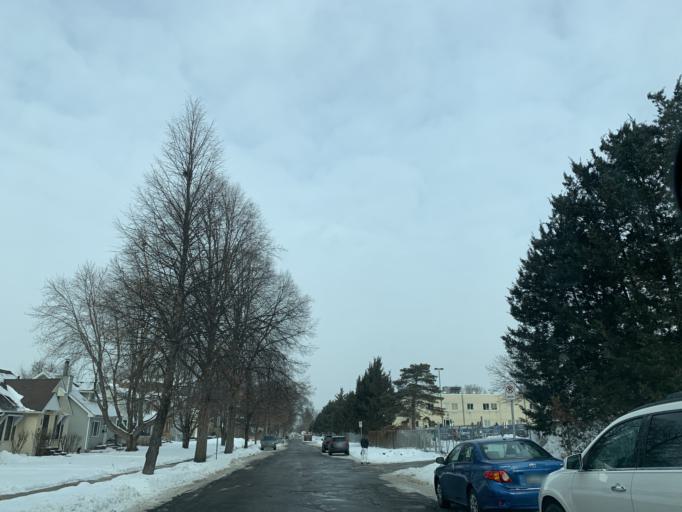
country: US
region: Minnesota
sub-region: Dakota County
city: Mendota Heights
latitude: 44.9020
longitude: -93.2076
